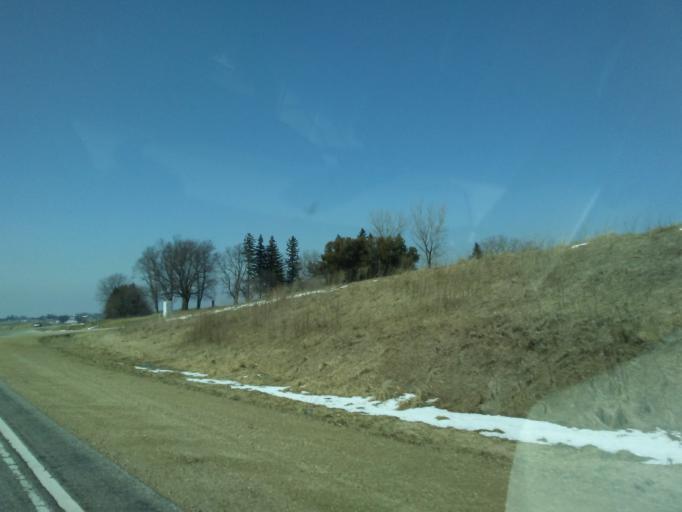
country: US
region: Wisconsin
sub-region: Vernon County
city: Westby
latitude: 43.6573
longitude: -90.9143
